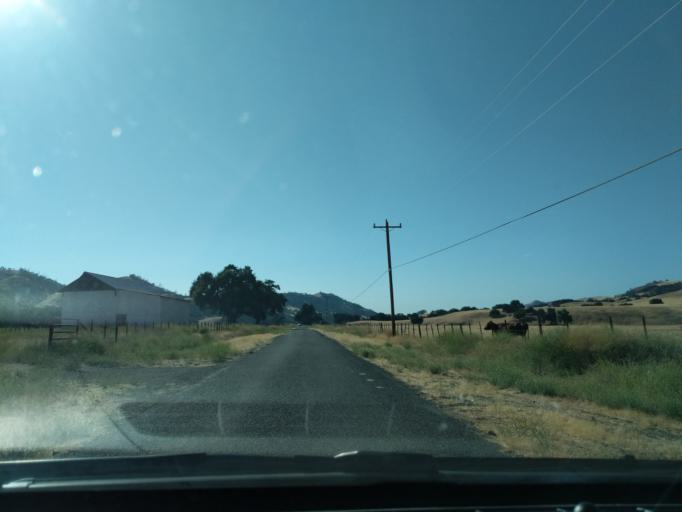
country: US
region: California
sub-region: San Luis Obispo County
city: San Miguel
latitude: 36.1134
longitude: -120.7227
